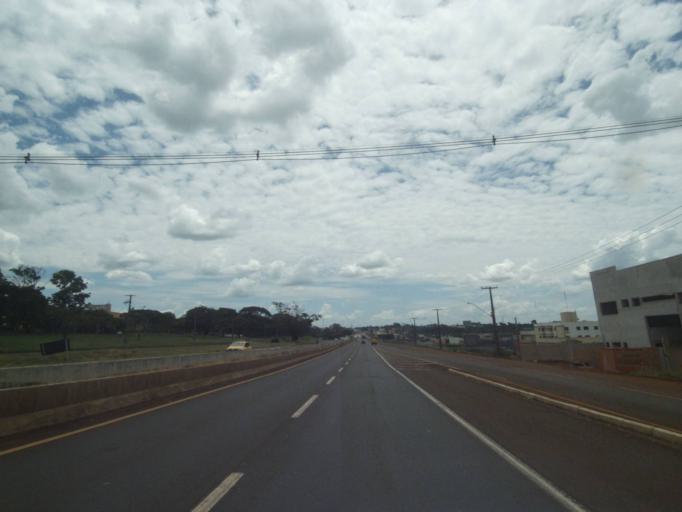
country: BR
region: Parana
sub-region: Londrina
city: Londrina
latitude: -23.3235
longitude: -51.1952
